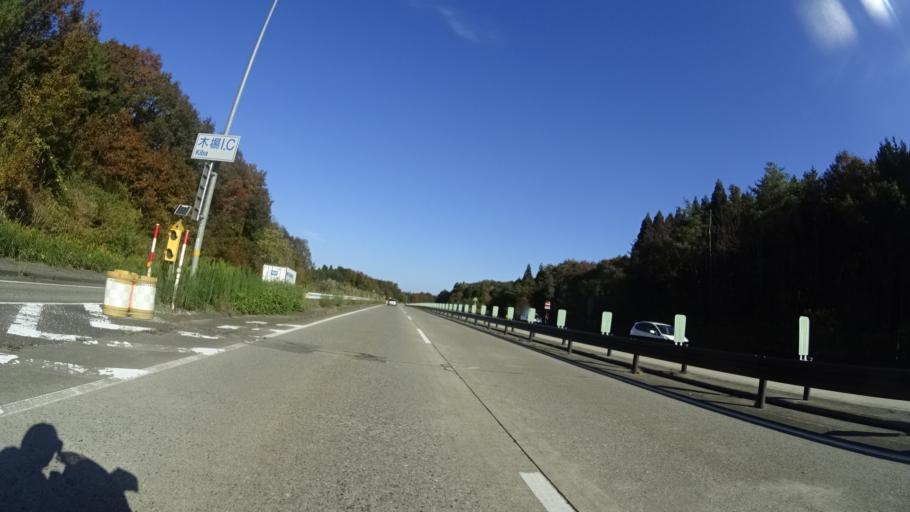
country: JP
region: Ishikawa
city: Komatsu
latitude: 36.3531
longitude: 136.4515
